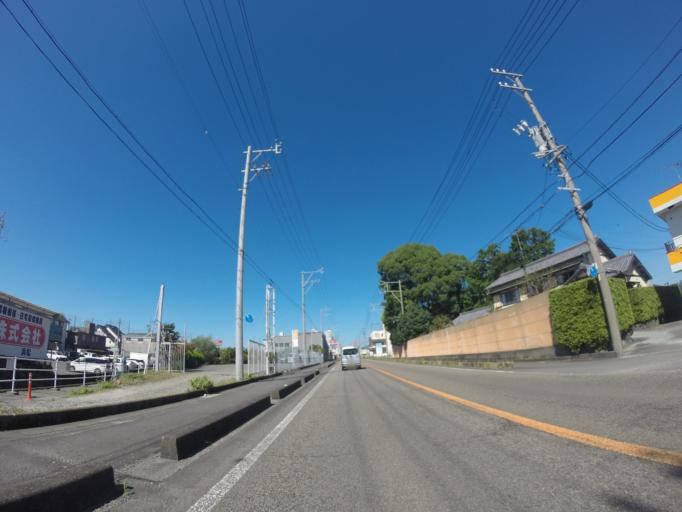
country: JP
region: Shizuoka
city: Shimada
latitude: 34.8360
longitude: 138.1871
